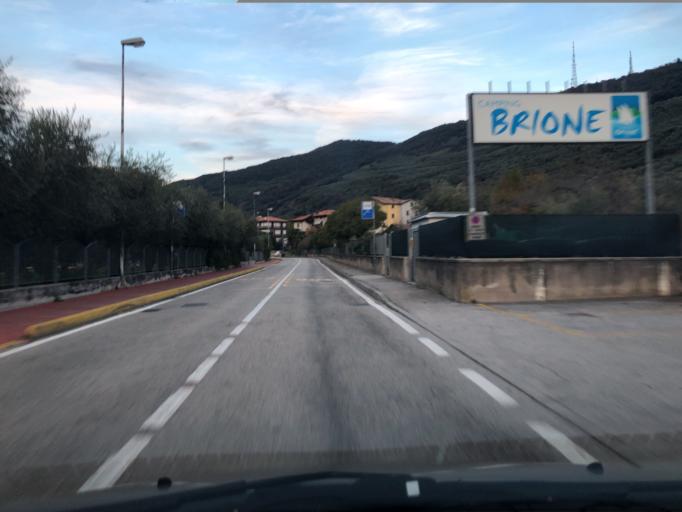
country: IT
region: Trentino-Alto Adige
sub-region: Provincia di Trento
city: Torbole sul Garda
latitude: 45.8812
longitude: 10.8615
